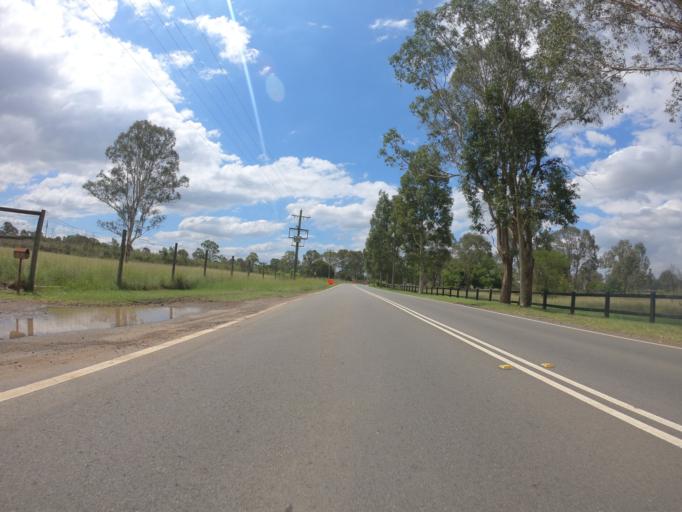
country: AU
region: New South Wales
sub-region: Penrith Municipality
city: Kingswood Park
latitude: -33.8302
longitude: 150.7581
